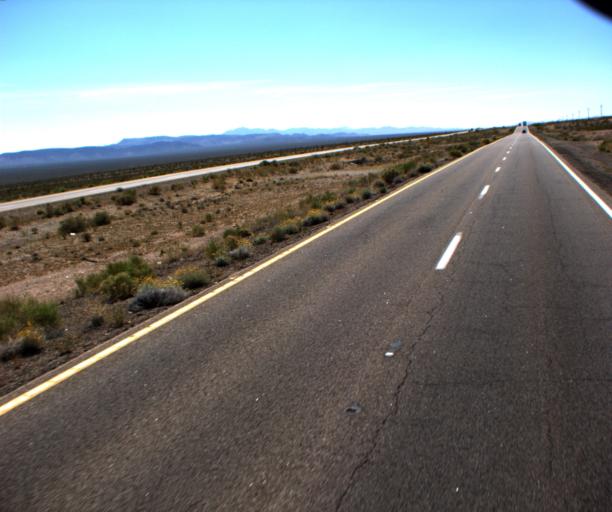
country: US
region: Arizona
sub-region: Mohave County
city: Dolan Springs
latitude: 35.7631
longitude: -114.5089
